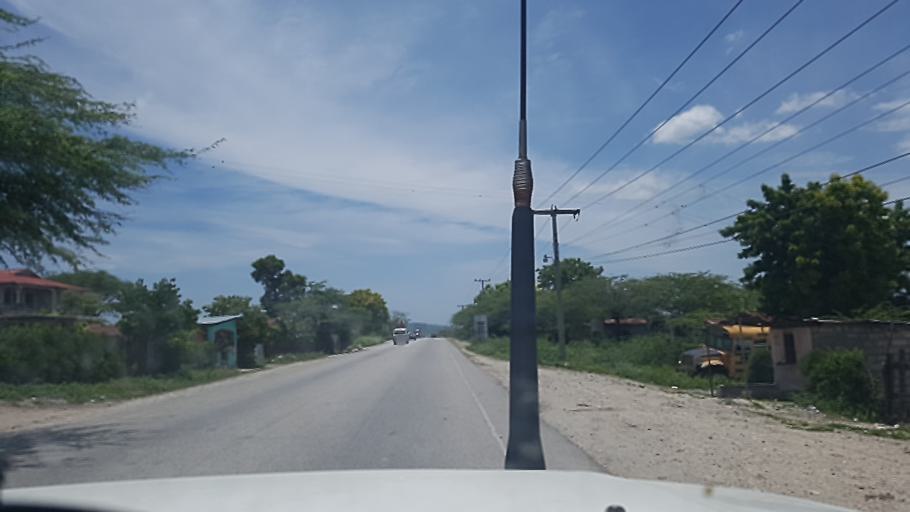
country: HT
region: Artibonite
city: Saint-Marc
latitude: 19.1517
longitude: -72.6262
